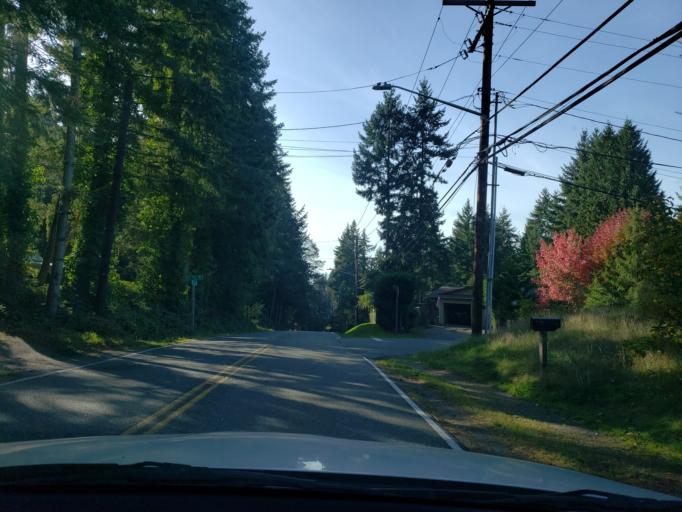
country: US
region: Washington
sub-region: Snohomish County
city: Meadowdale
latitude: 47.8644
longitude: -122.3107
